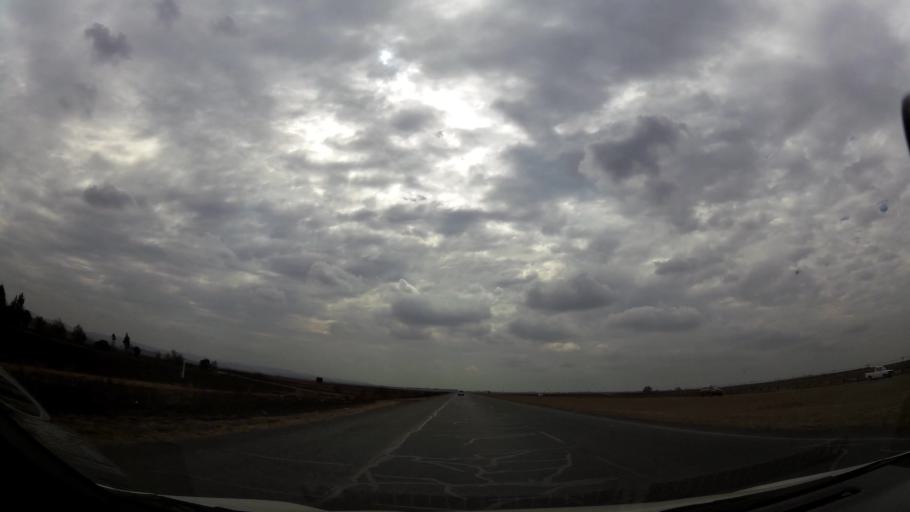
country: ZA
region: Gauteng
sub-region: Sedibeng District Municipality
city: Meyerton
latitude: -26.3964
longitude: 28.0820
